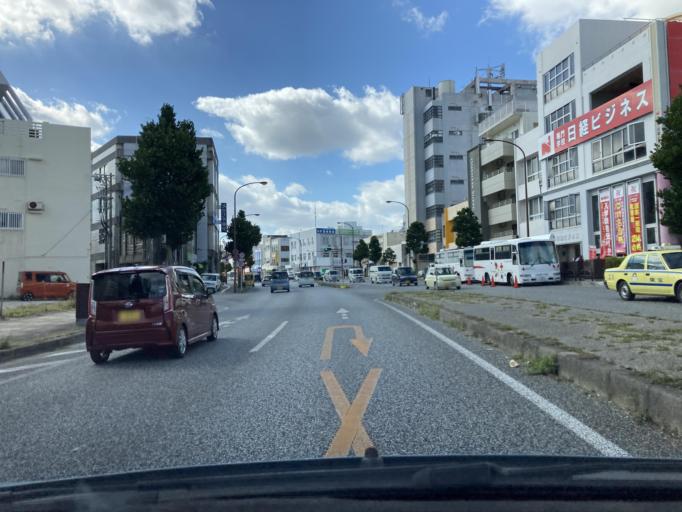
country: JP
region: Okinawa
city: Okinawa
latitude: 26.3296
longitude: 127.7948
